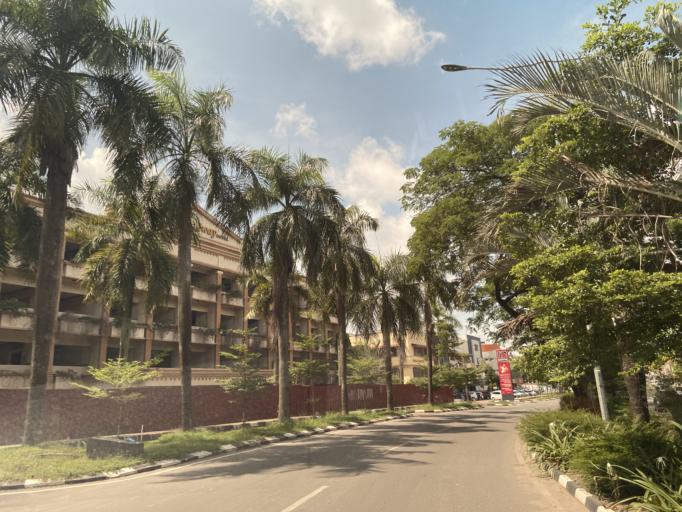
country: SG
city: Singapore
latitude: 1.1500
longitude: 104.0092
